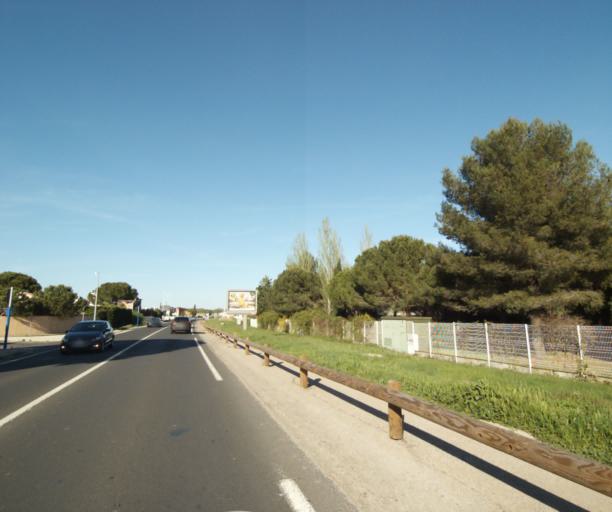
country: FR
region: Languedoc-Roussillon
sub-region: Departement de l'Herault
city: Perols
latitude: 43.5880
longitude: 3.9310
